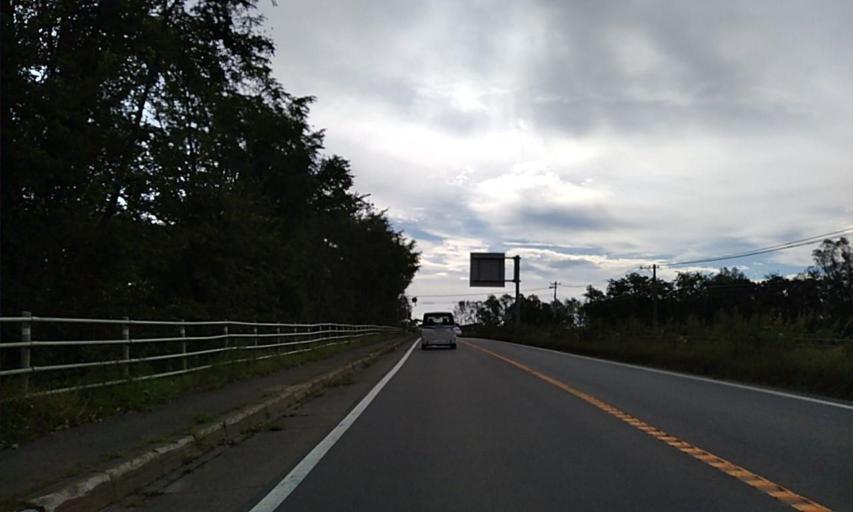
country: JP
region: Hokkaido
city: Obihiro
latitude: 42.8420
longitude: 143.1829
